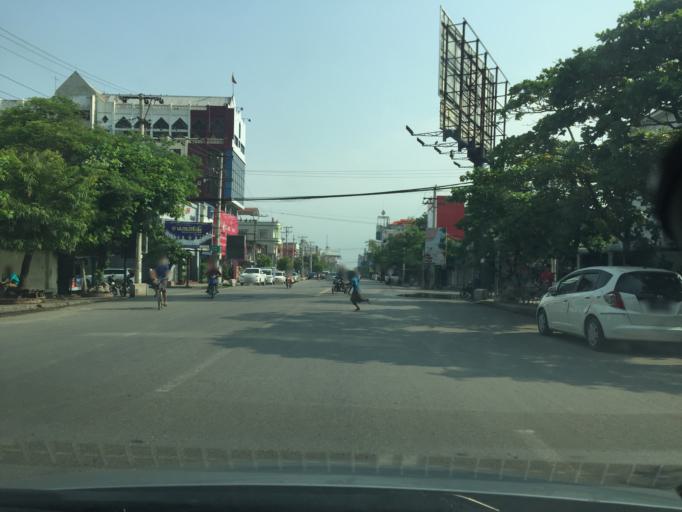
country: MM
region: Mandalay
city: Mandalay
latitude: 21.9705
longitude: 96.0837
